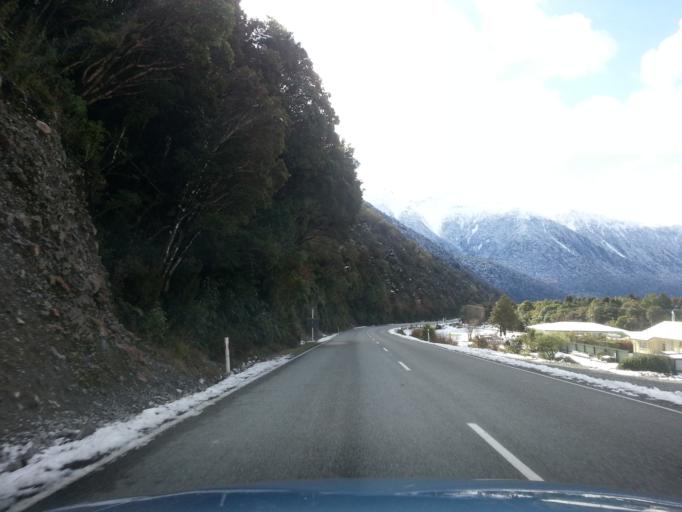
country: NZ
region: West Coast
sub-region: Grey District
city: Greymouth
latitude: -42.8307
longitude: 171.5611
